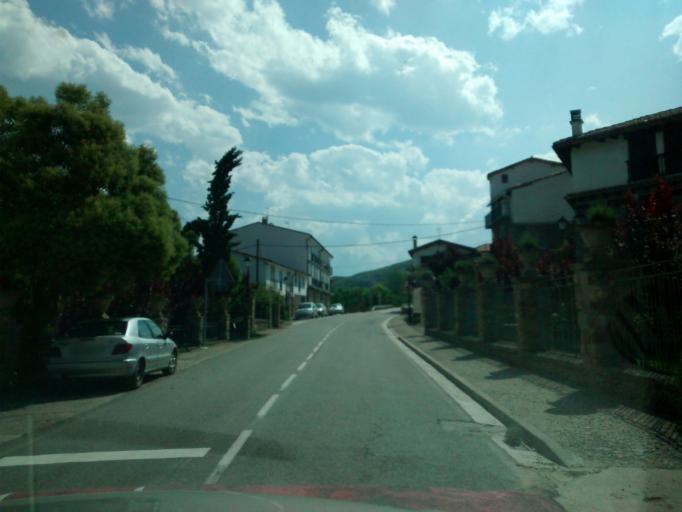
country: ES
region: La Rioja
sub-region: Provincia de La Rioja
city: San Roman de Cameros
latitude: 42.2308
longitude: -2.4748
